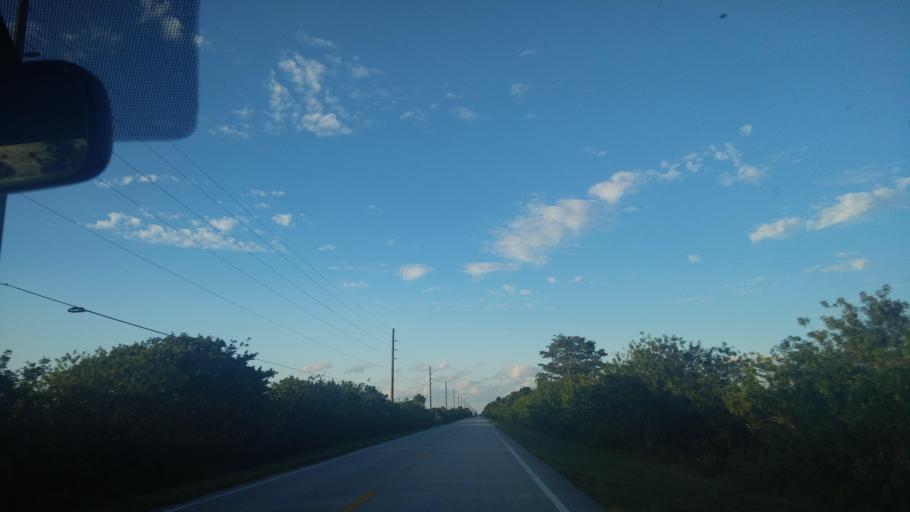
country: US
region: Florida
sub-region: Indian River County
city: Fellsmere
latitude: 27.6727
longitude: -80.6431
